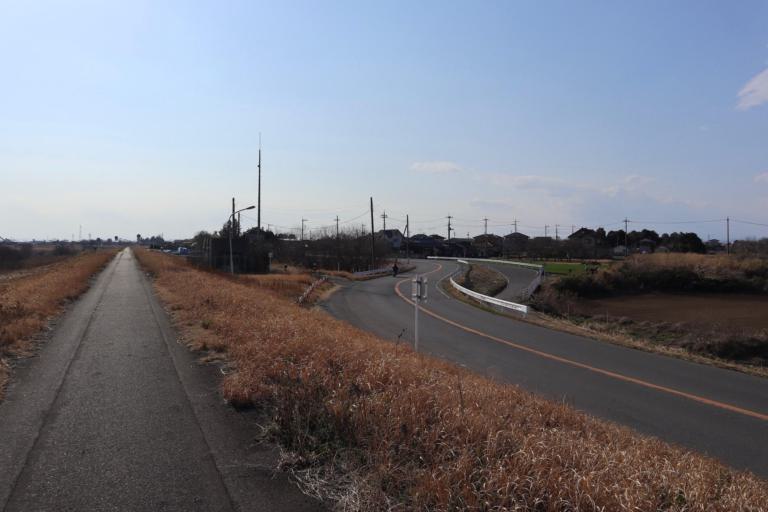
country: JP
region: Tochigi
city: Fujioka
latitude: 36.2660
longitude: 139.6636
